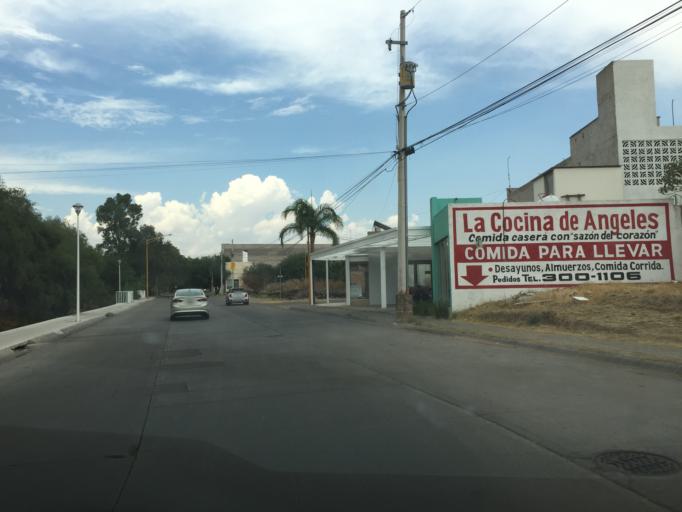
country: MX
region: Aguascalientes
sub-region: Jesus Maria
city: El Llano
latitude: 21.9302
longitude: -102.3014
